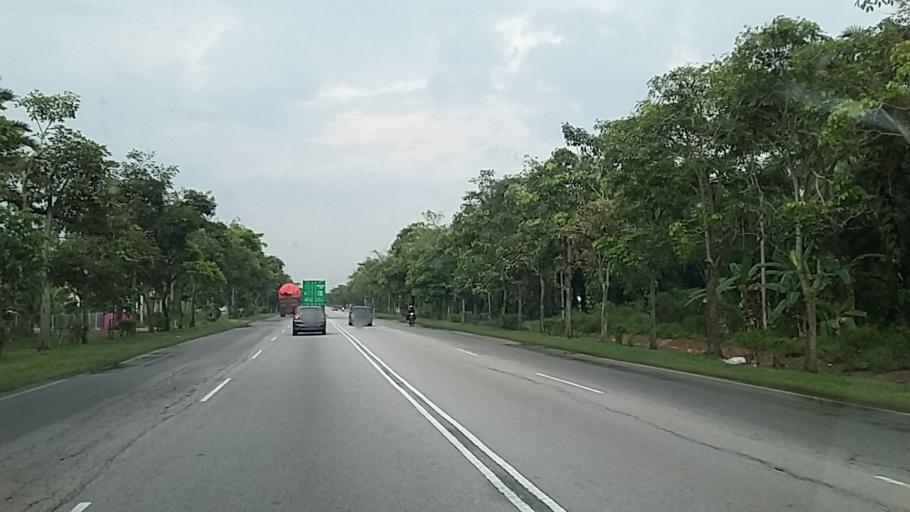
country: MY
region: Johor
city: Parit Raja
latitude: 1.8731
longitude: 103.1352
